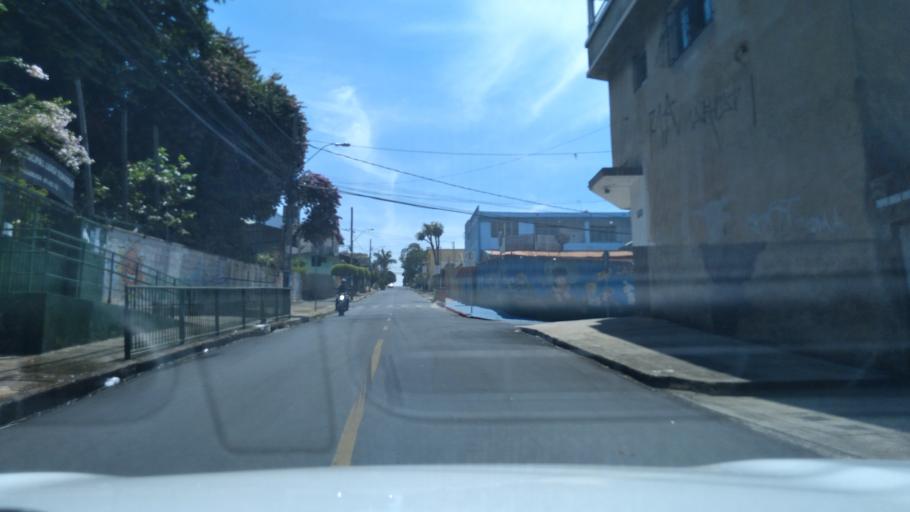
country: BR
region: Minas Gerais
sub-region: Contagem
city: Contagem
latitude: -19.9026
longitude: -44.0177
